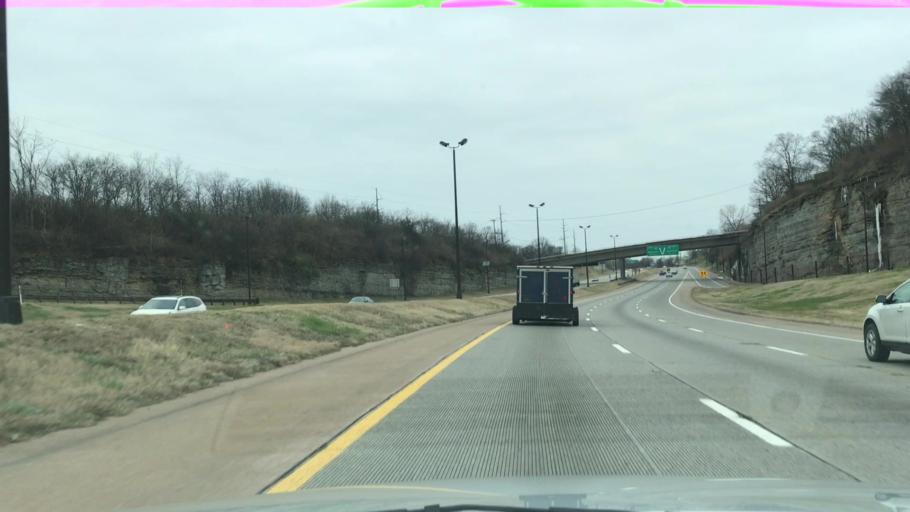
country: US
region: Tennessee
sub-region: Davidson County
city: Nashville
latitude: 36.1405
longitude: -86.8229
